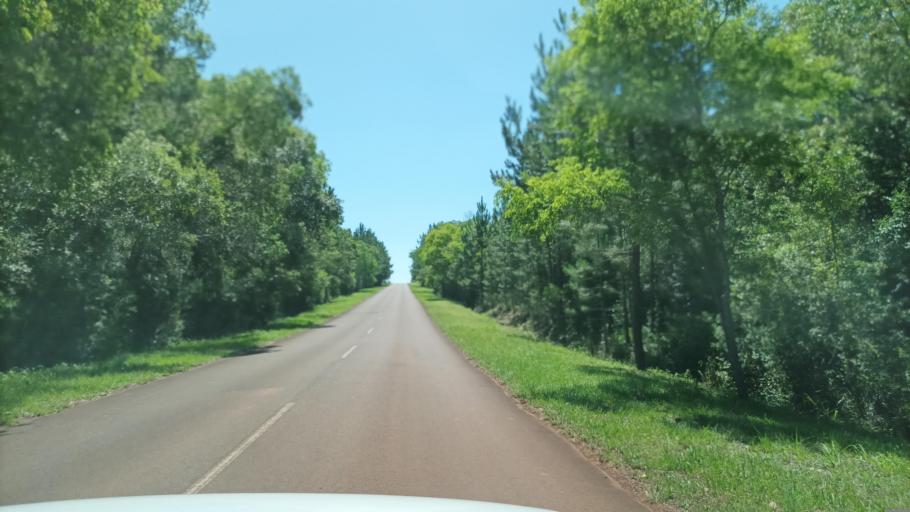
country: AR
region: Misiones
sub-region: Departamento de Apostoles
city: San Jose
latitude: -27.7754
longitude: -55.7345
